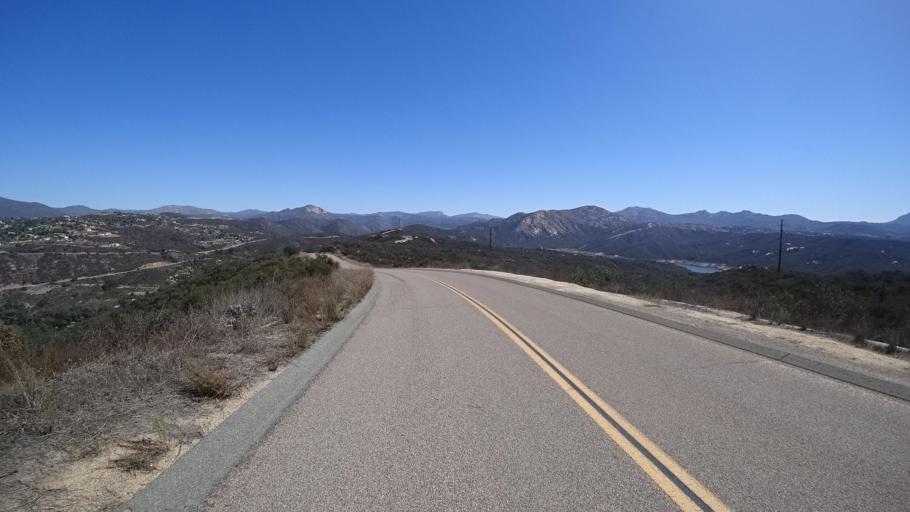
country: US
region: California
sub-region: San Diego County
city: Alpine
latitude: 32.7988
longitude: -116.7891
